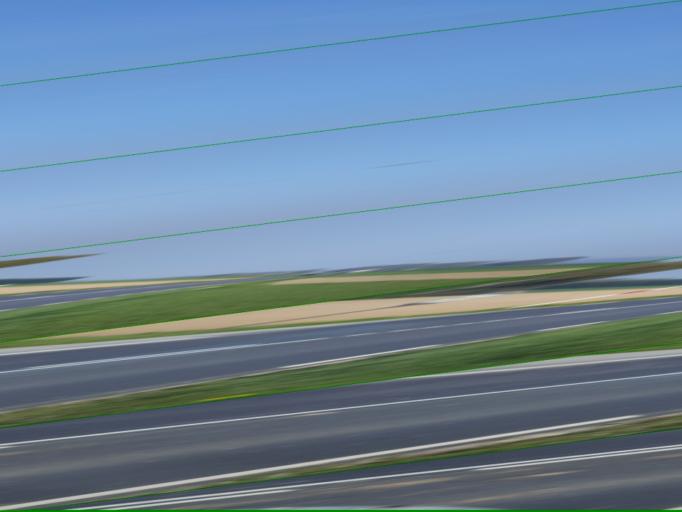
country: FR
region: Ile-de-France
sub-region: Departement des Yvelines
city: Guerville
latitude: 48.9320
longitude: 1.7247
